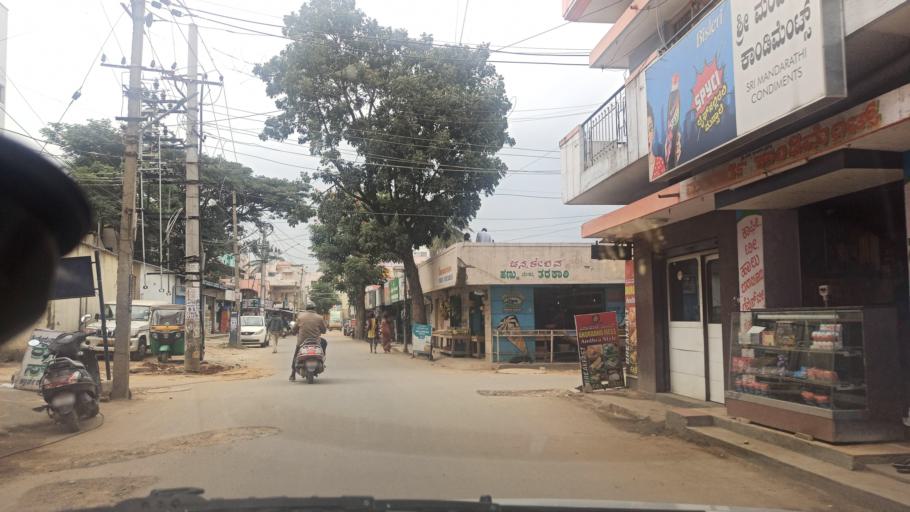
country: IN
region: Karnataka
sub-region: Bangalore Urban
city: Yelahanka
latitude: 13.0373
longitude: 77.5920
